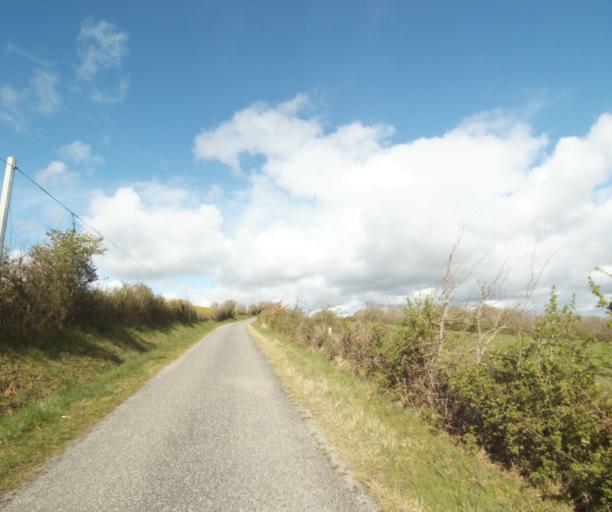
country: FR
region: Midi-Pyrenees
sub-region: Departement de l'Ariege
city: Saverdun
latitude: 43.2288
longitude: 1.5293
